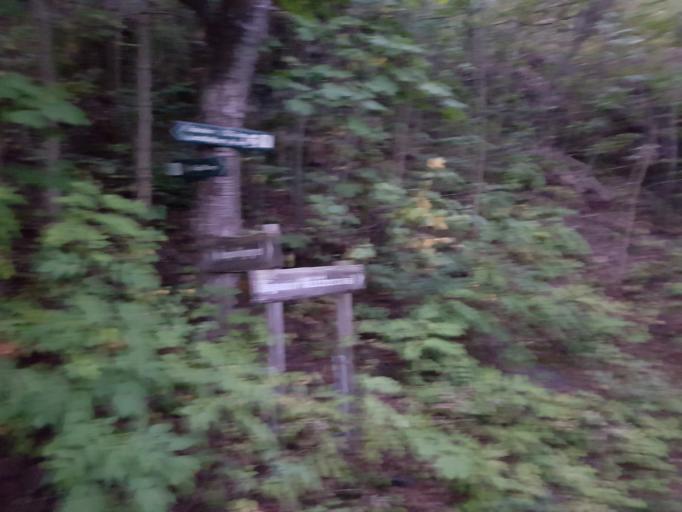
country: NO
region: Buskerud
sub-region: Drammen
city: Drammen
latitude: 59.7510
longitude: 10.2044
